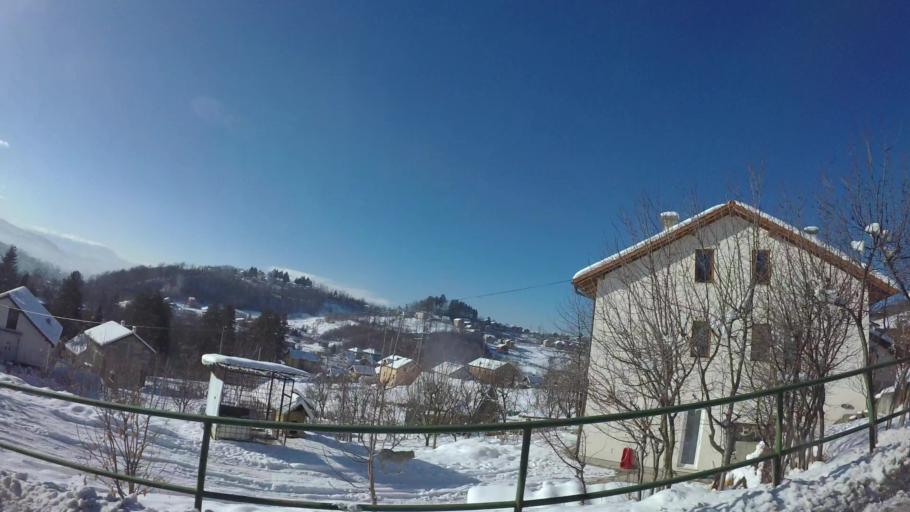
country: BA
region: Federation of Bosnia and Herzegovina
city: Kobilja Glava
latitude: 43.8930
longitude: 18.4166
